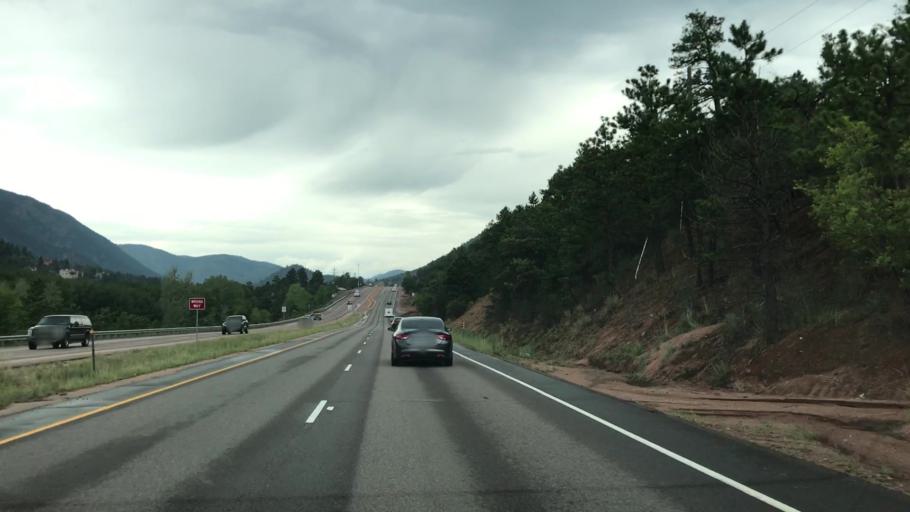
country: US
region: Colorado
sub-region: El Paso County
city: Cascade-Chipita Park
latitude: 38.9088
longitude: -104.9727
